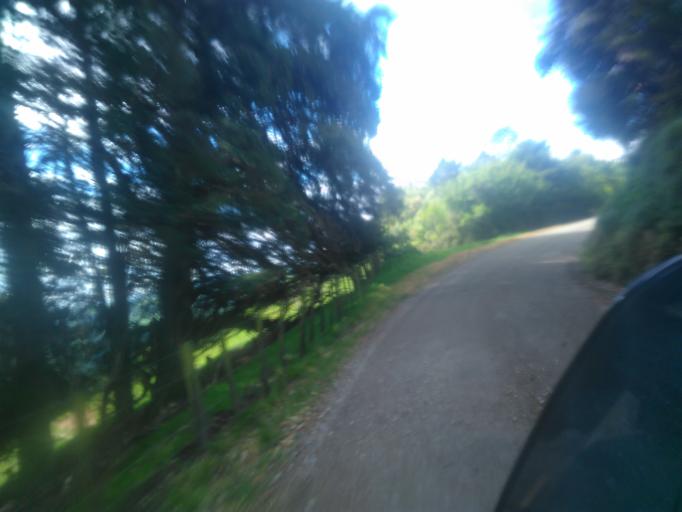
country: NZ
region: Hawke's Bay
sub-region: Wairoa District
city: Wairoa
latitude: -38.7726
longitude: 177.6377
